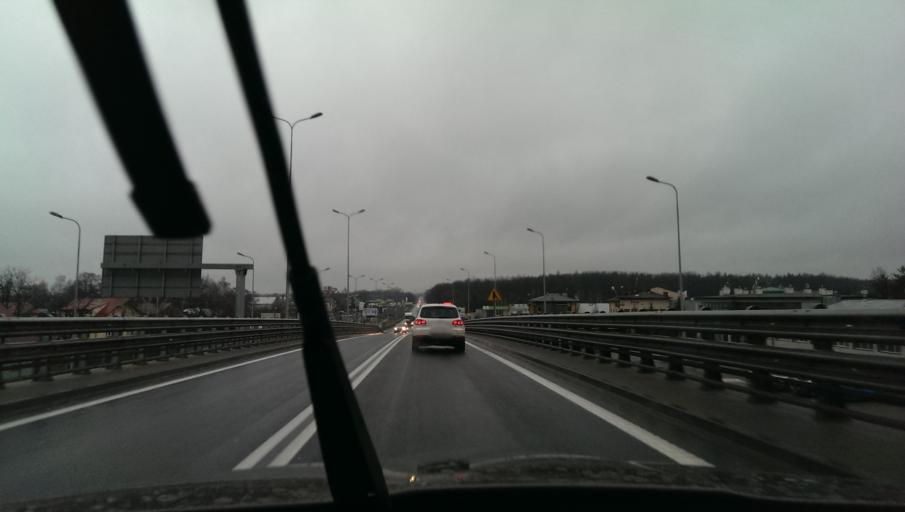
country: PL
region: Subcarpathian Voivodeship
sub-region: Powiat rzeszowski
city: Rudna Mala
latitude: 50.1151
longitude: 21.9728
